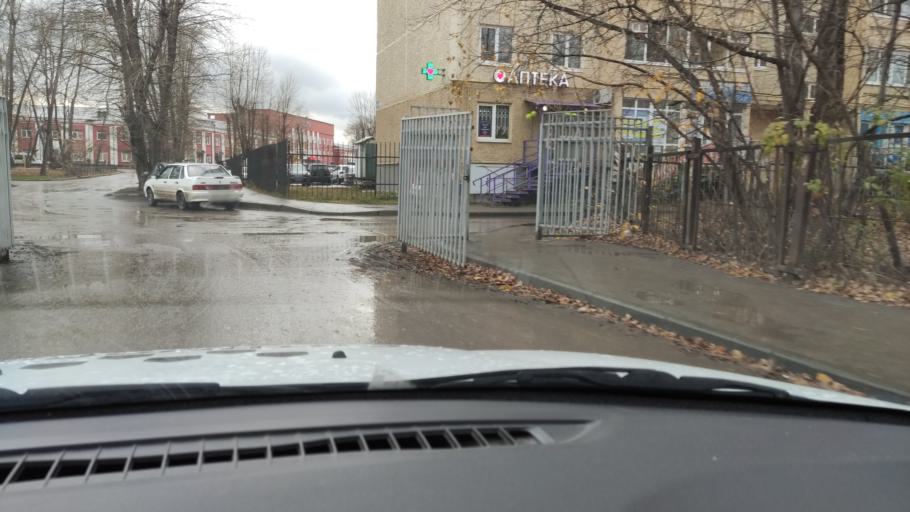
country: RU
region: Perm
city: Perm
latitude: 57.9681
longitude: 56.2659
